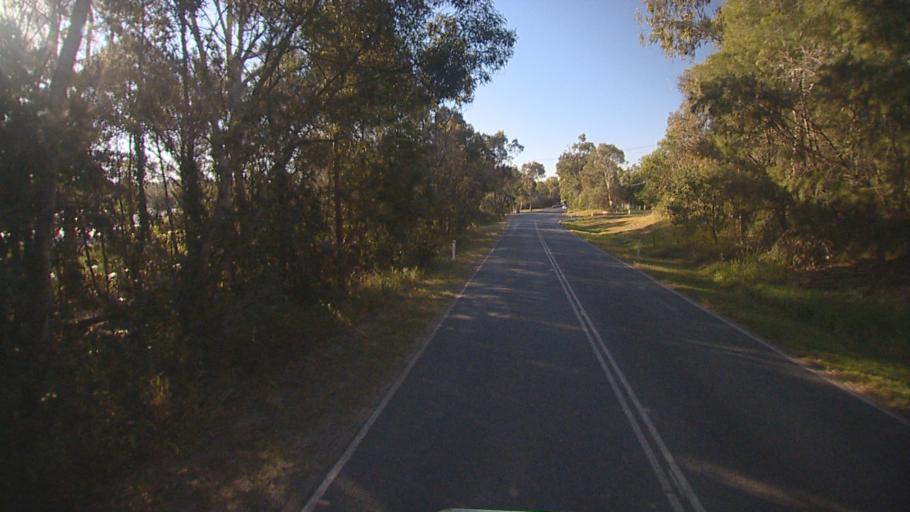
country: AU
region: Queensland
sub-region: Logan
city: Logan Reserve
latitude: -27.7245
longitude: 153.0901
